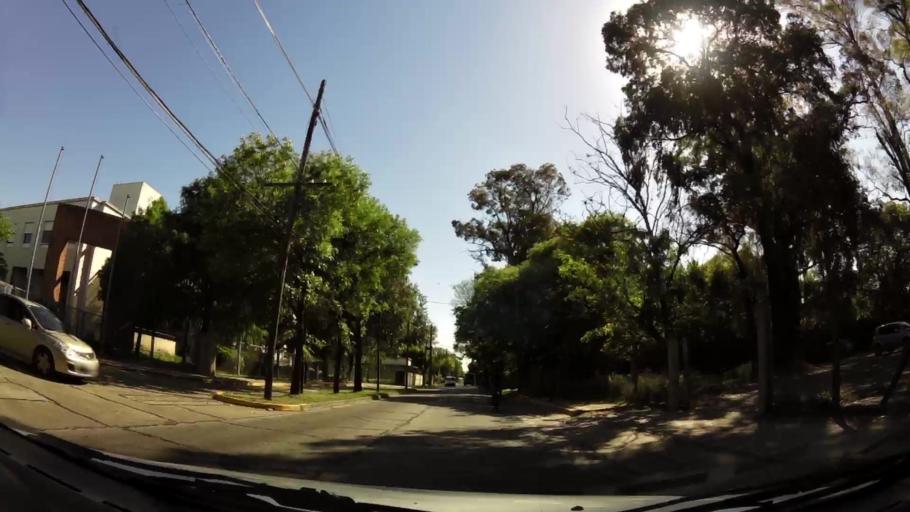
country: AR
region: Buenos Aires
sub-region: Partido de San Isidro
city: San Isidro
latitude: -34.4760
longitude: -58.5446
